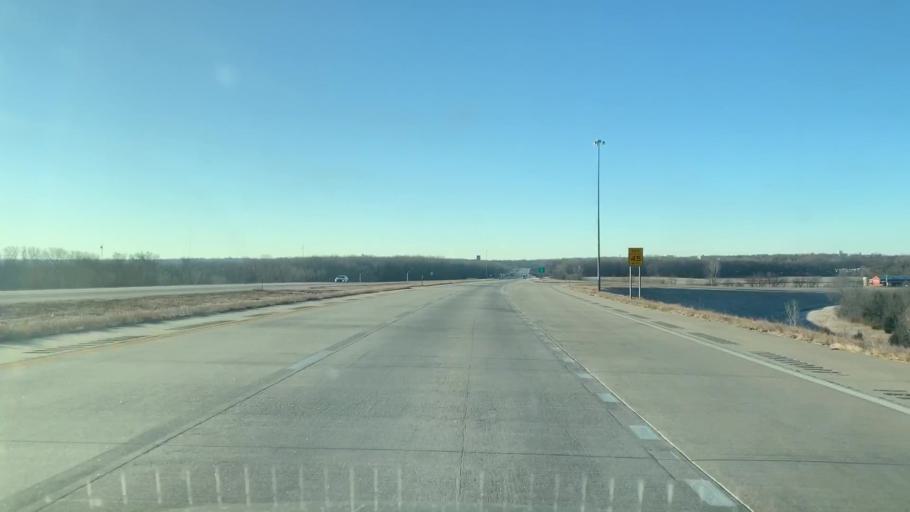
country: US
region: Kansas
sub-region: Bourbon County
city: Fort Scott
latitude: 37.8594
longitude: -94.7027
